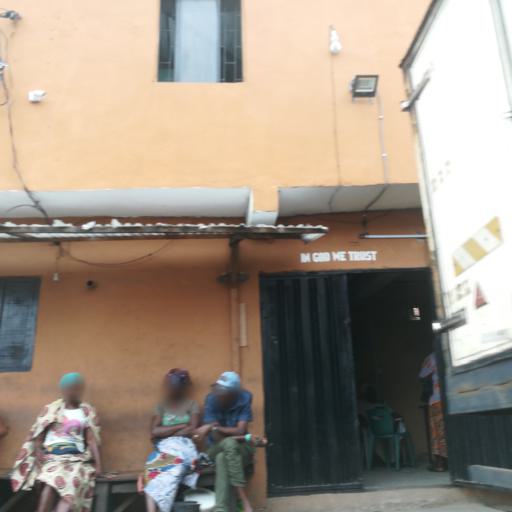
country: NG
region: Lagos
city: Makoko
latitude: 6.4964
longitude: 3.3878
